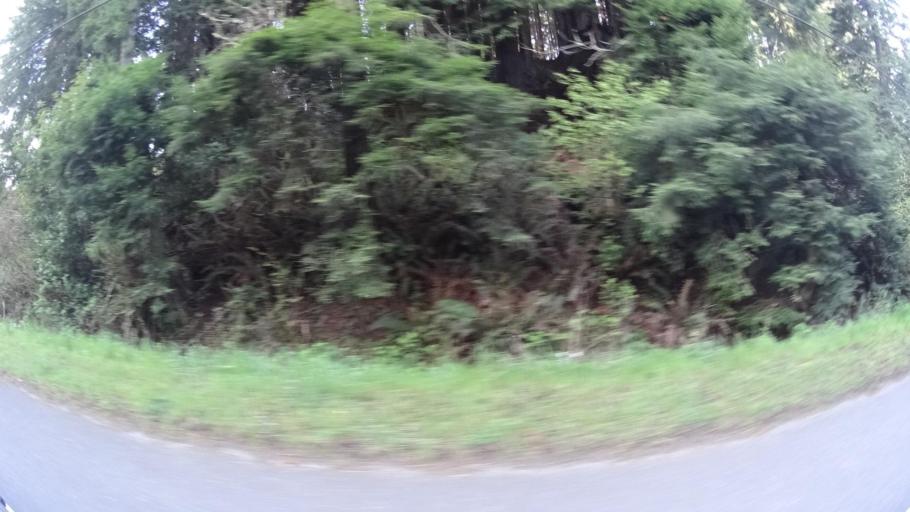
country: US
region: California
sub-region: Humboldt County
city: Myrtletown
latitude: 40.7625
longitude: -124.0628
